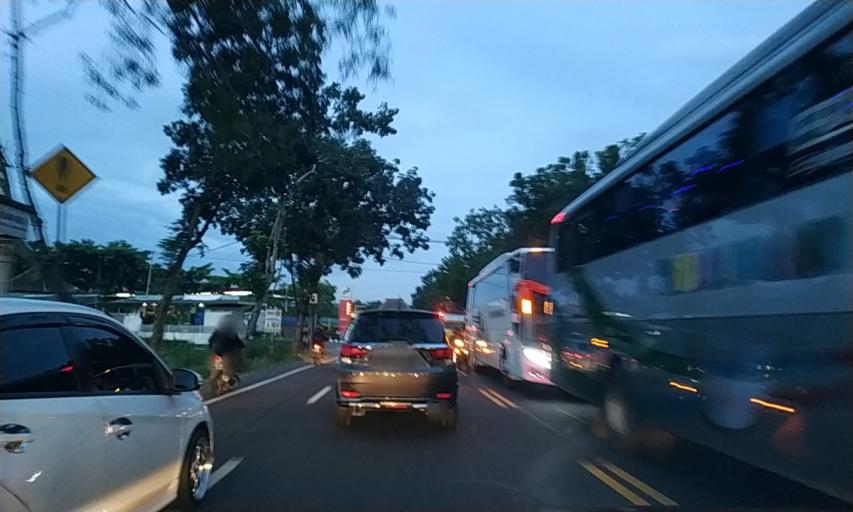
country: ID
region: Daerah Istimewa Yogyakarta
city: Godean
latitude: -7.8265
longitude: 110.2252
